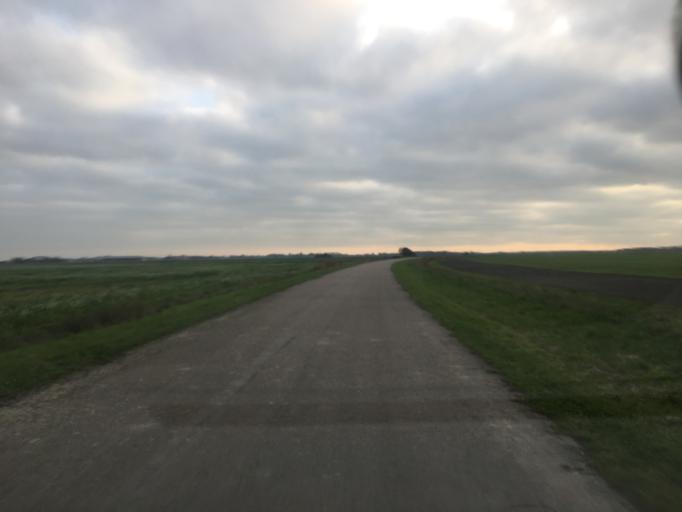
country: DE
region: Schleswig-Holstein
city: Aventoft
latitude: 54.9245
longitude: 8.7710
